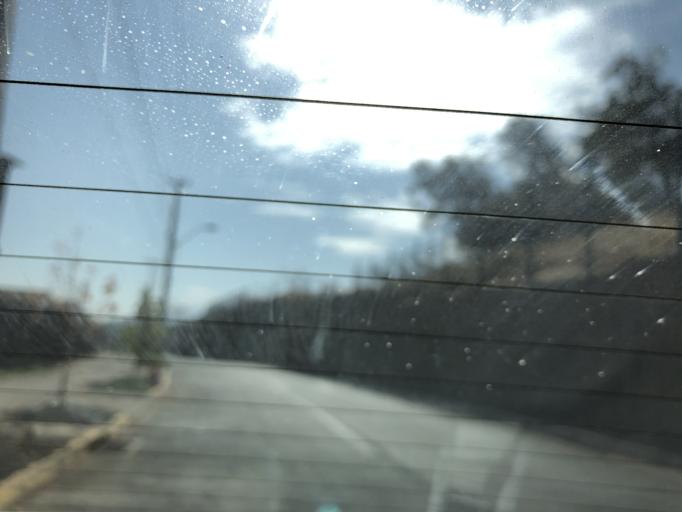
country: CL
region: Santiago Metropolitan
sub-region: Provincia de Cordillera
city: Puente Alto
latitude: -33.5716
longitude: -70.5401
